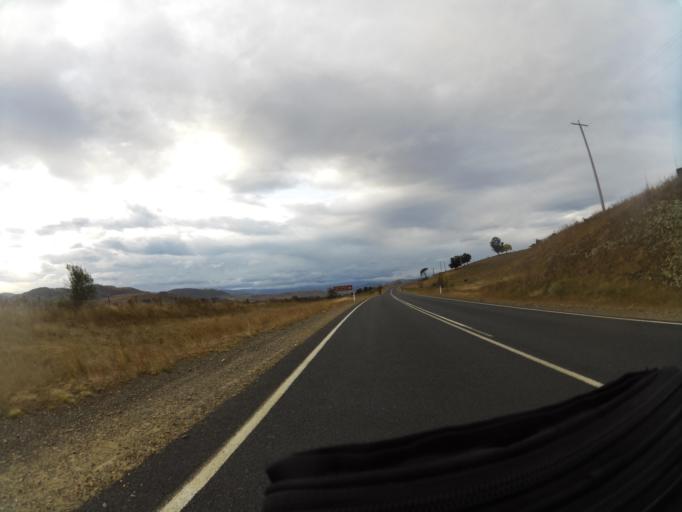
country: AU
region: New South Wales
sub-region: Snowy River
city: Jindabyne
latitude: -36.0815
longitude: 147.9760
